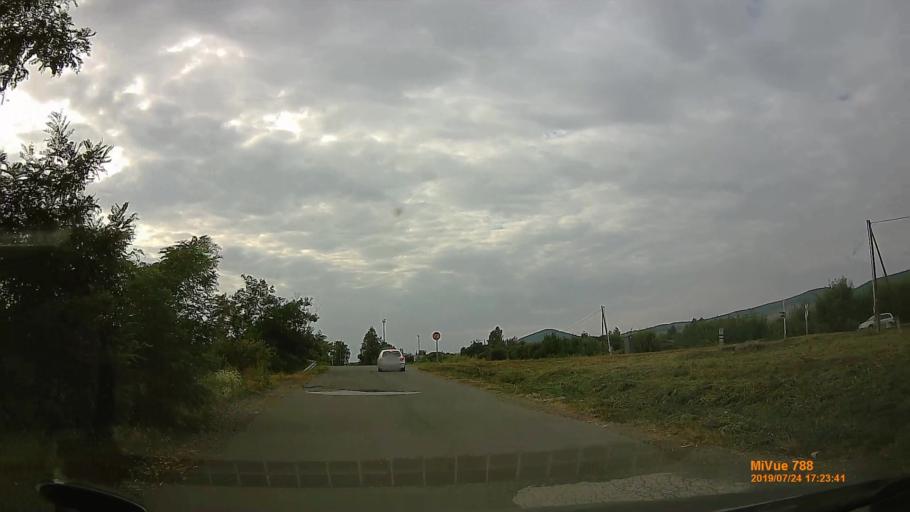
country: HU
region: Borsod-Abauj-Zemplen
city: Tallya
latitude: 48.2243
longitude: 21.2270
